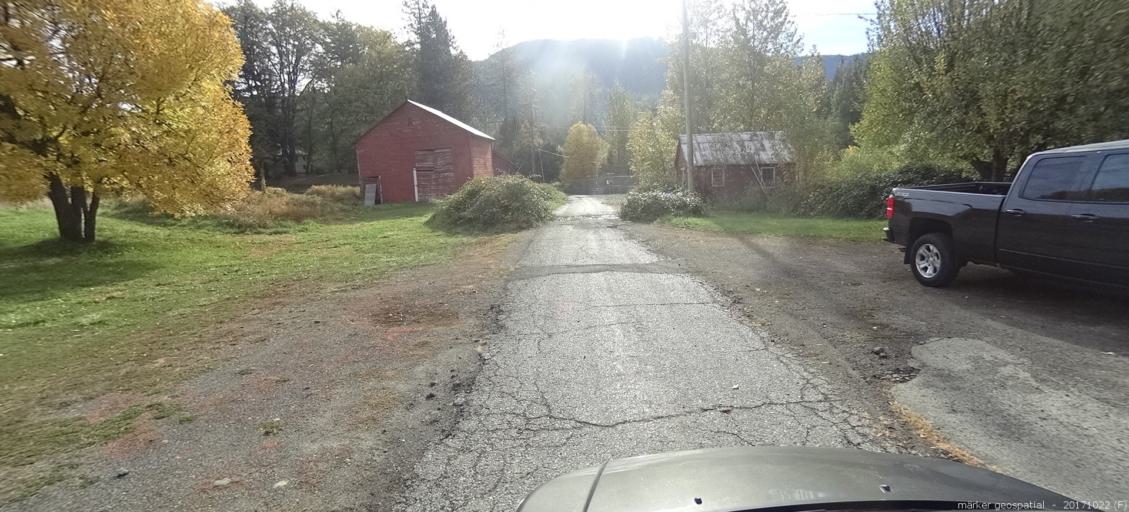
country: US
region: California
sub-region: Siskiyou County
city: Dunsmuir
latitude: 41.1467
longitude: -122.3203
